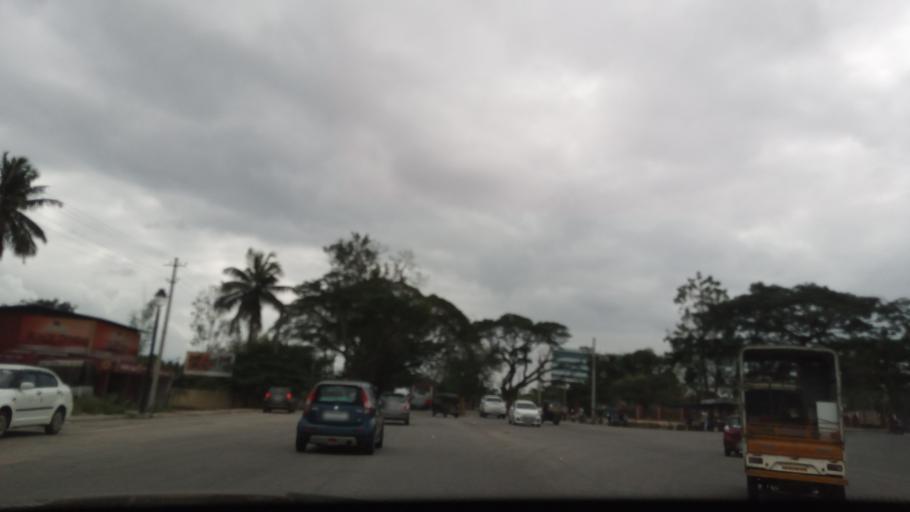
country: IN
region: Karnataka
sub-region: Mysore
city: Mysore
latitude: 12.3480
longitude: 76.6602
